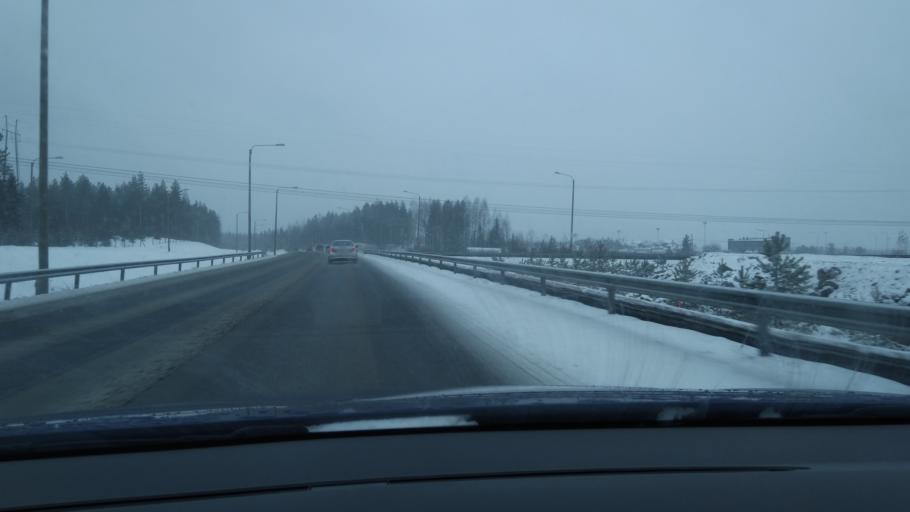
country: FI
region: Pirkanmaa
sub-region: Tampere
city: Kangasala
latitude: 61.5379
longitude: 23.9776
